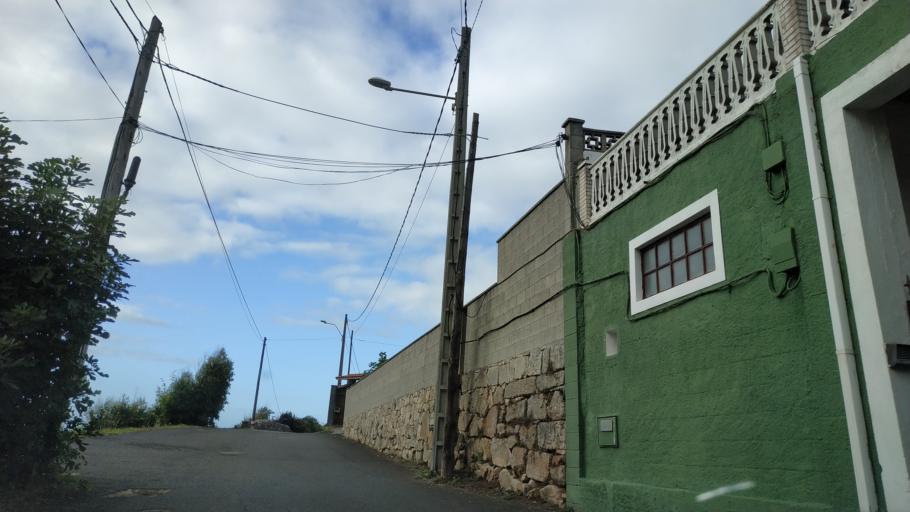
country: ES
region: Galicia
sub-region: Provincia da Coruna
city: A Coruna
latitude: 43.3725
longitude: -8.4456
